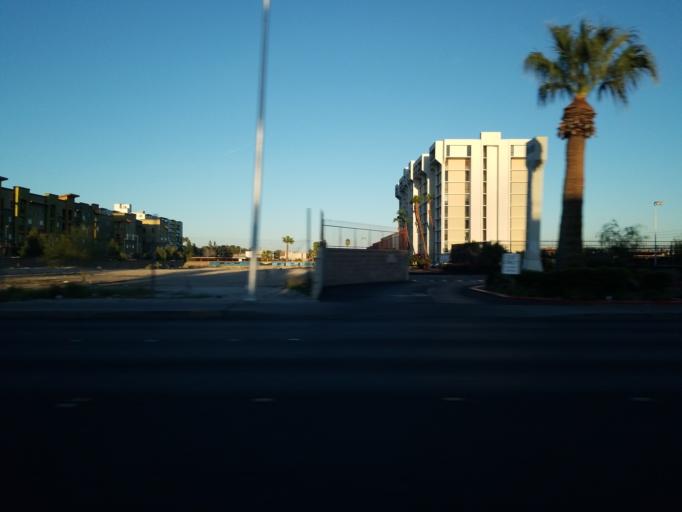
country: US
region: Nevada
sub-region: Clark County
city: Paradise
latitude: 36.1181
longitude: -115.1463
